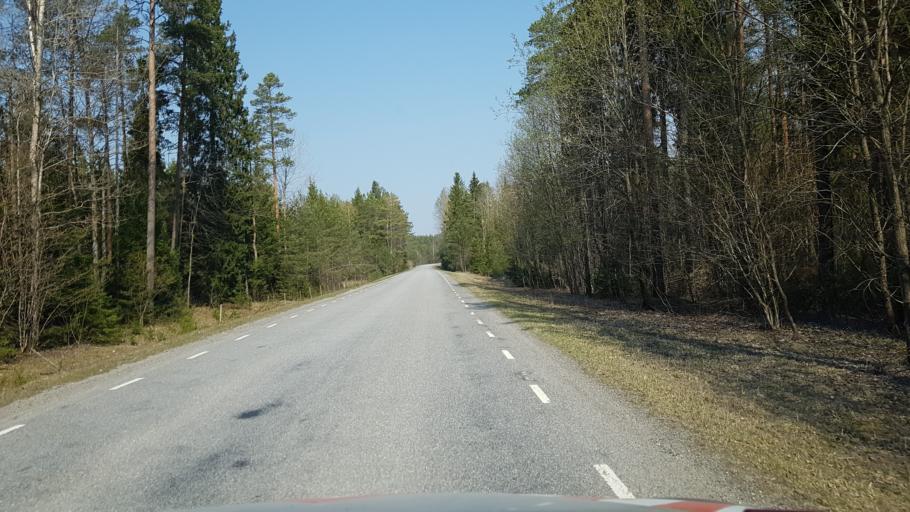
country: EE
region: Raplamaa
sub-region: Kohila vald
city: Kohila
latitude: 59.1904
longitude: 24.6622
